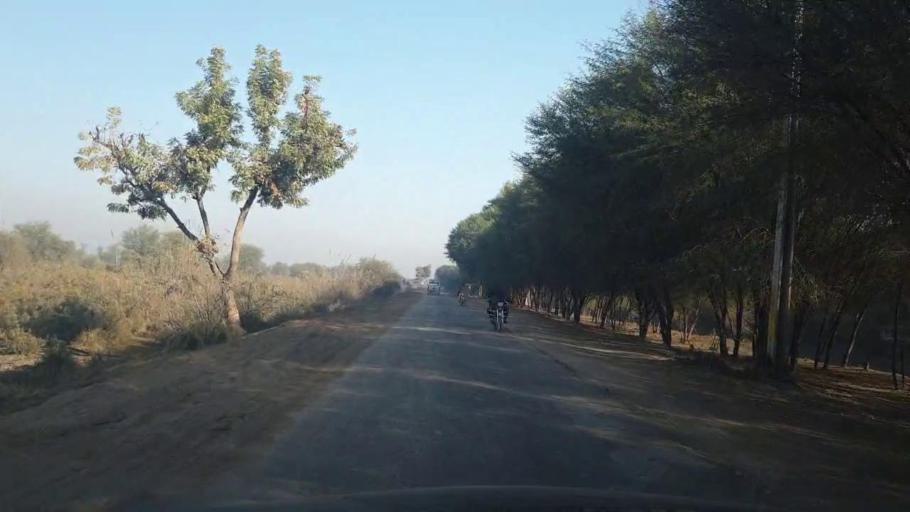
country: PK
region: Sindh
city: Mirpur Mathelo
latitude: 28.0655
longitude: 69.4653
